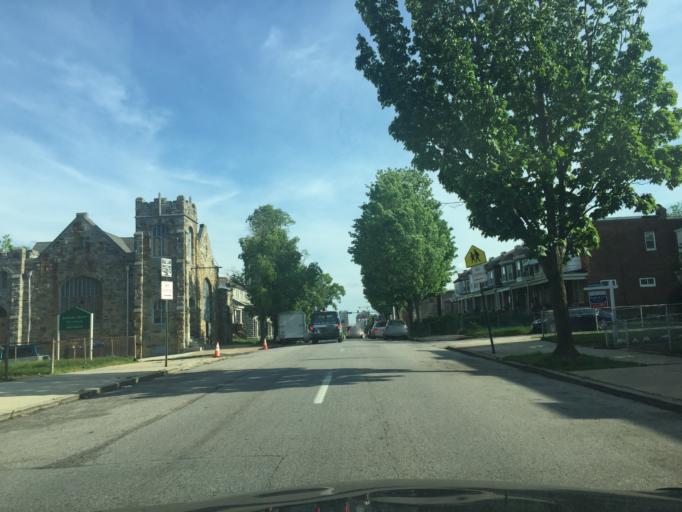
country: US
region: Maryland
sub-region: City of Baltimore
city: Baltimore
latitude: 39.3135
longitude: -76.5918
